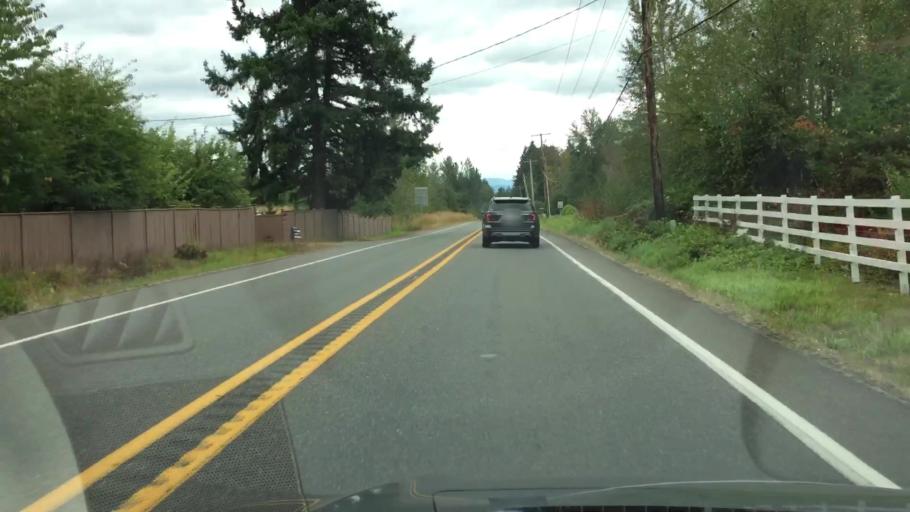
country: US
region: Washington
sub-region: Pierce County
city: Graham
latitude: 47.0151
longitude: -122.2964
